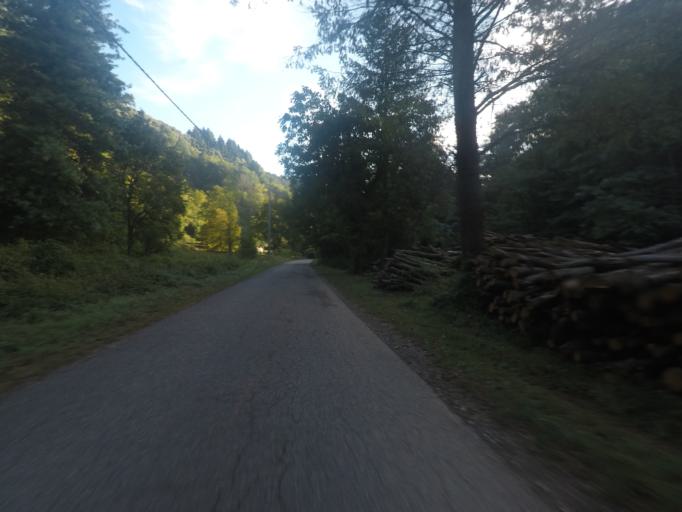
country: IT
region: Tuscany
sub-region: Provincia di Lucca
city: Pescaglia
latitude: 43.9511
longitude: 10.4180
